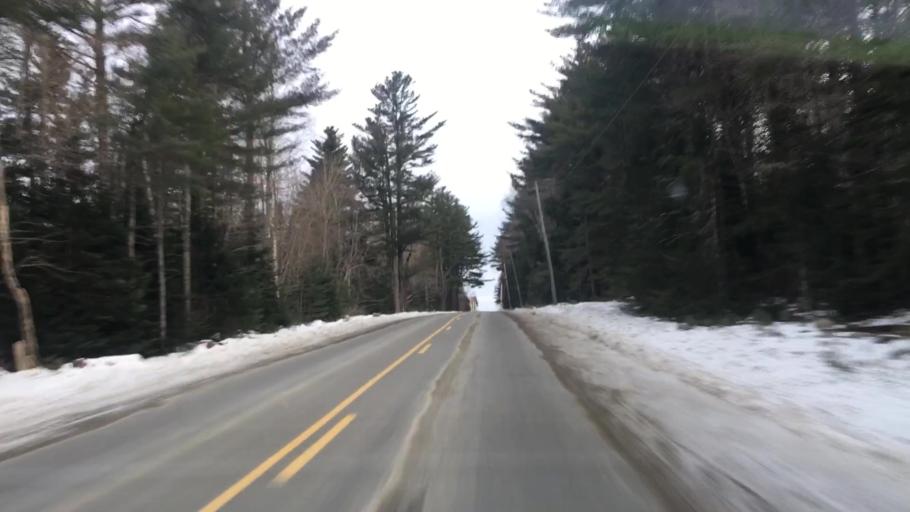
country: US
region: Maine
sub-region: Hancock County
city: Franklin
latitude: 44.7644
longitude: -68.3254
